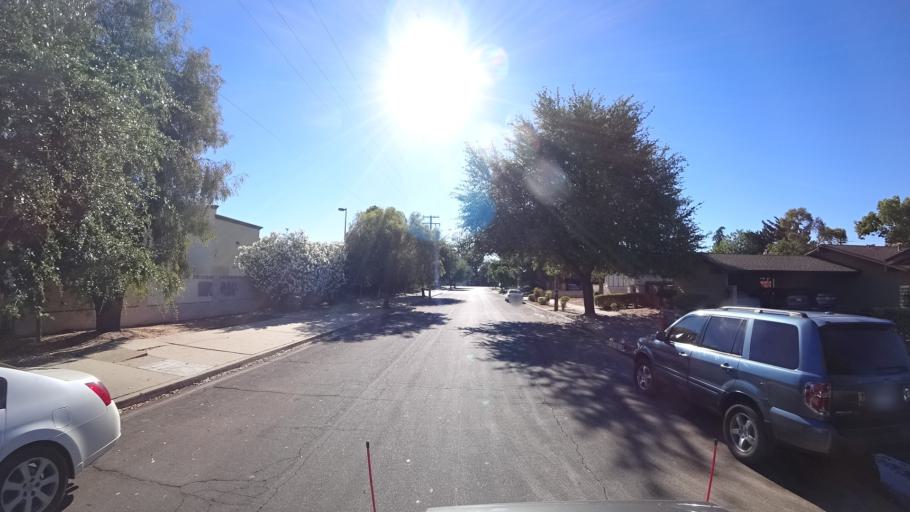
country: US
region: California
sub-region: Fresno County
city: Fresno
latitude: 36.8070
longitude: -119.8282
